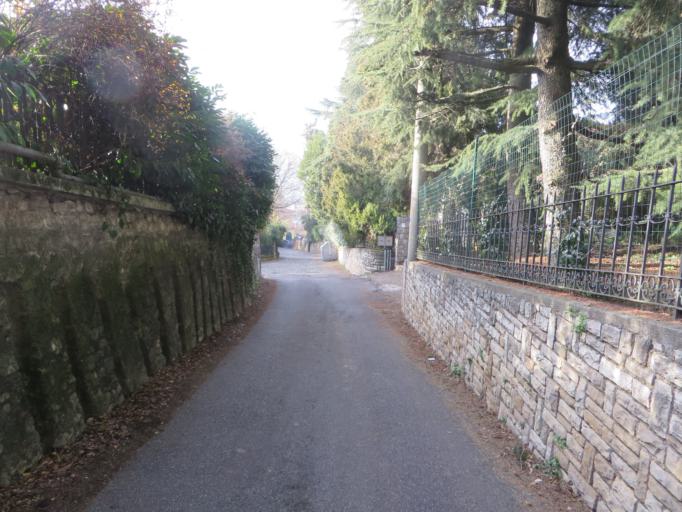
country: IT
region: Lombardy
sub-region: Provincia di Brescia
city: Brescia
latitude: 45.5347
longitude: 10.2502
